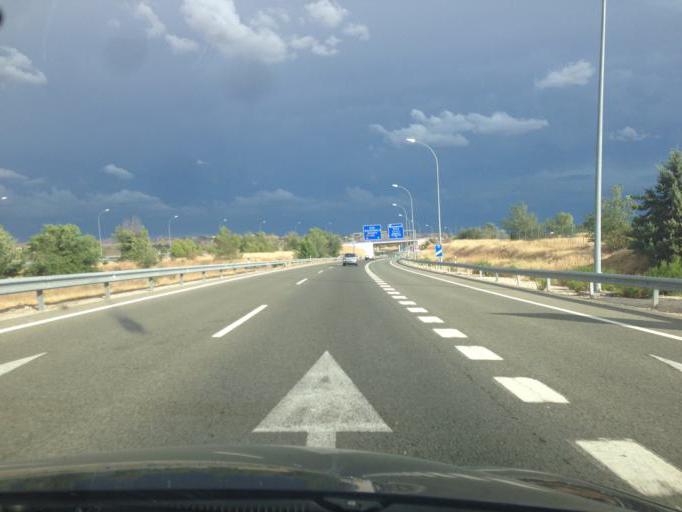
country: ES
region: Madrid
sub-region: Provincia de Madrid
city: San Sebastian de los Reyes
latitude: 40.5474
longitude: -3.5747
